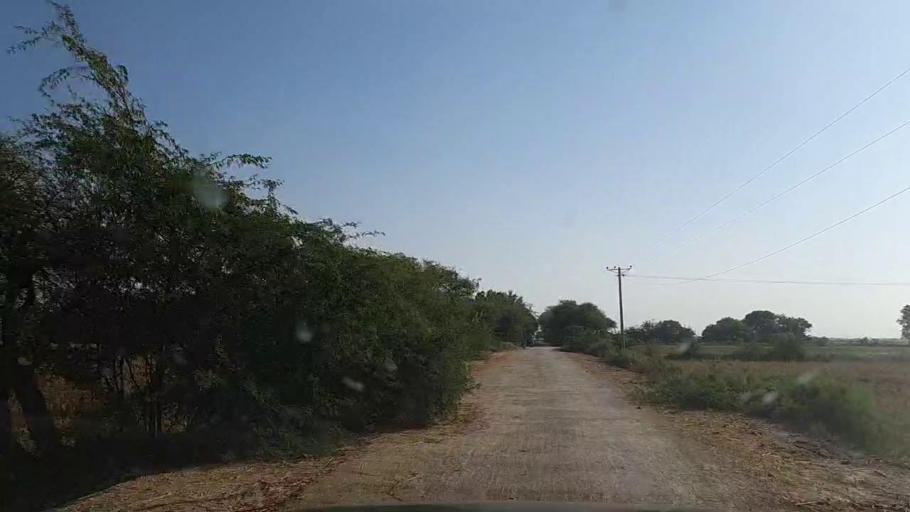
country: PK
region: Sindh
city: Daro Mehar
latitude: 24.6465
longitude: 68.0751
